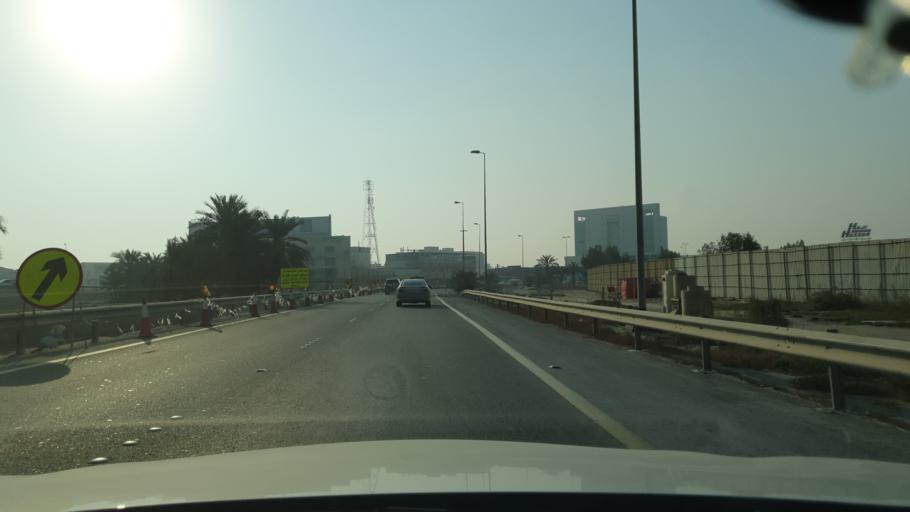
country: BH
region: Northern
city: Madinat `Isa
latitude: 26.1934
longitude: 50.5342
